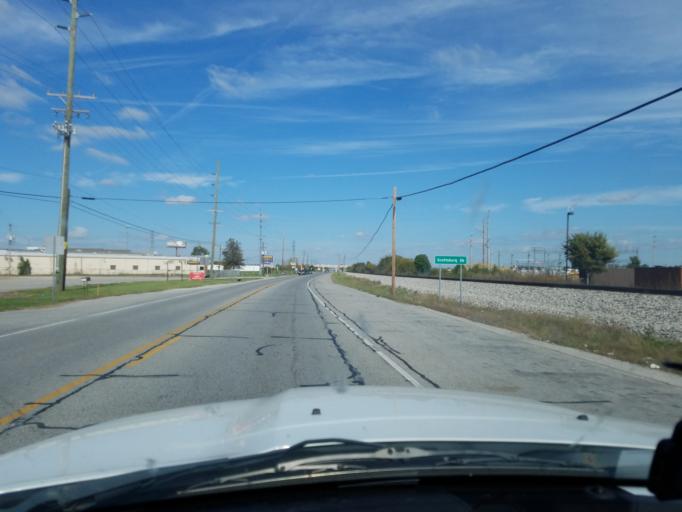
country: US
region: Indiana
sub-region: Clark County
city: Clarksville
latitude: 38.3222
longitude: -85.7513
